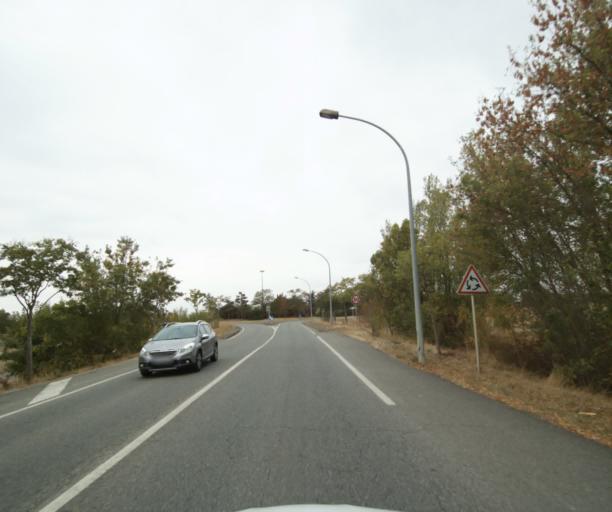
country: FR
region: Midi-Pyrenees
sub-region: Departement de la Haute-Garonne
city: Villefranche-de-Lauragais
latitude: 43.4006
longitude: 1.7013
